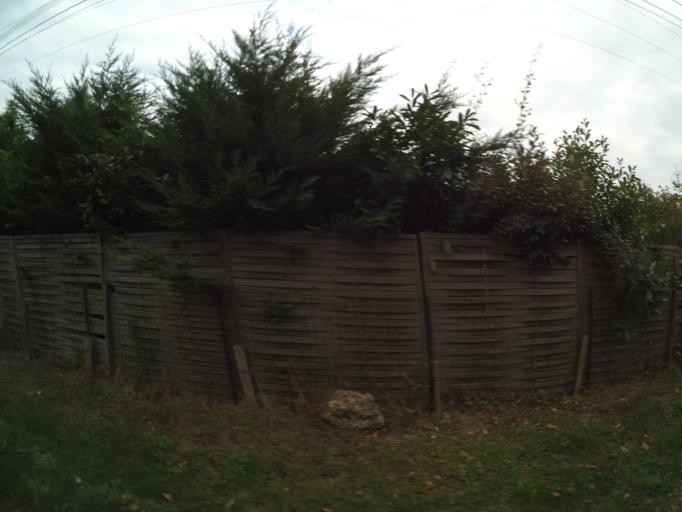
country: FR
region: Centre
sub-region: Departement d'Indre-et-Loire
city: Reugny
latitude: 47.4806
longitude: 0.9109
